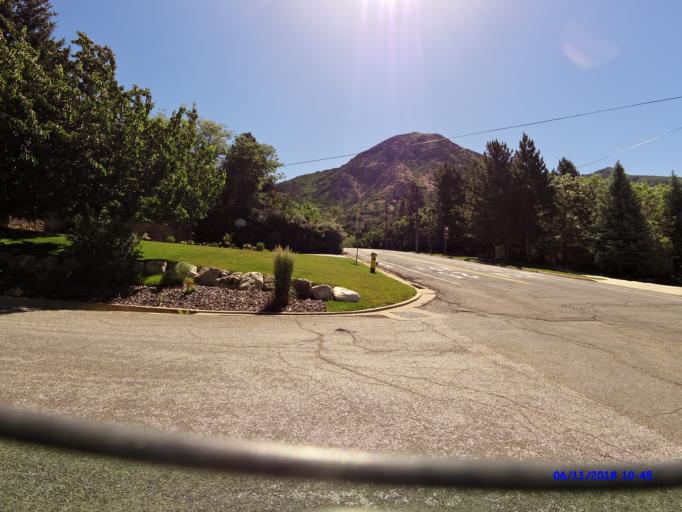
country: US
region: Utah
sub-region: Weber County
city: Ogden
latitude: 41.2119
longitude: -111.9371
